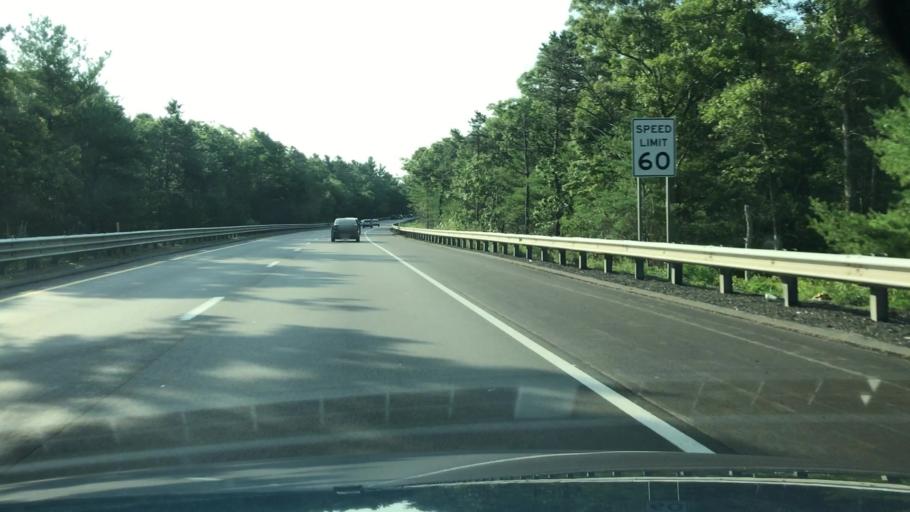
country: US
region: Massachusetts
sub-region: Plymouth County
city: Plymouth
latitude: 41.9278
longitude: -70.6353
